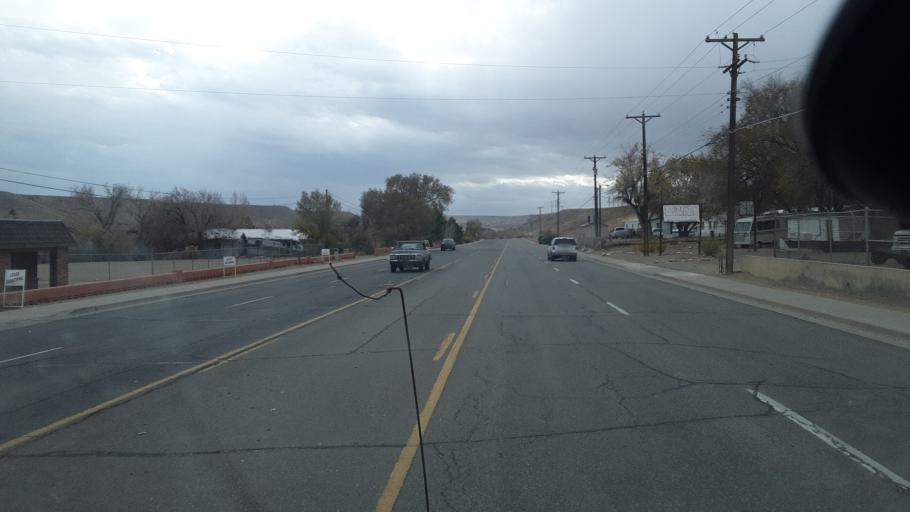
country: US
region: New Mexico
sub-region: San Juan County
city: Farmington
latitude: 36.7529
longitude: -108.2439
